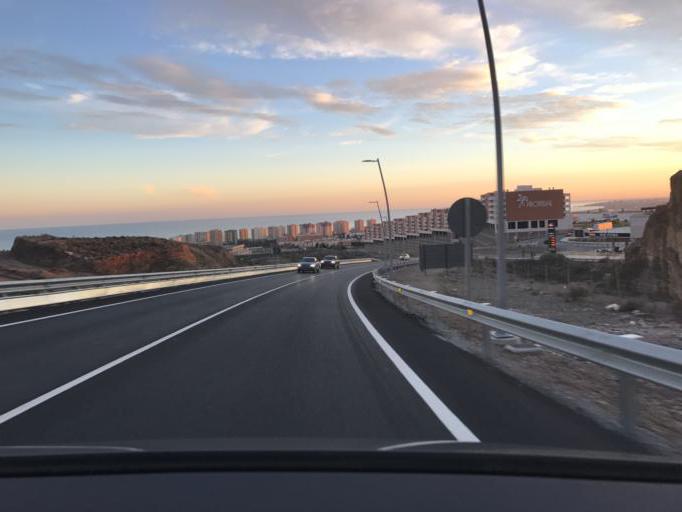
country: ES
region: Andalusia
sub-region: Provincia de Almeria
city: Aguadulce
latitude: 36.8243
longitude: -2.5819
